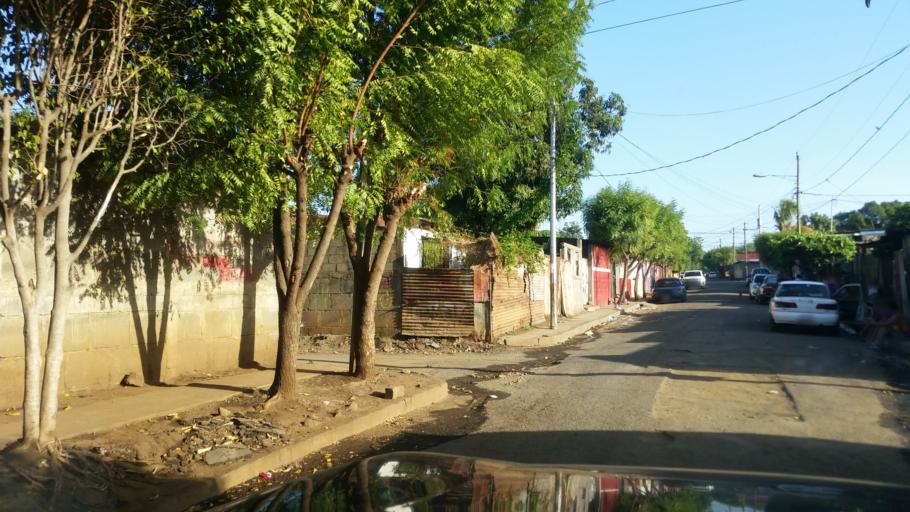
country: NI
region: Managua
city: Managua
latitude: 12.1319
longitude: -86.2889
